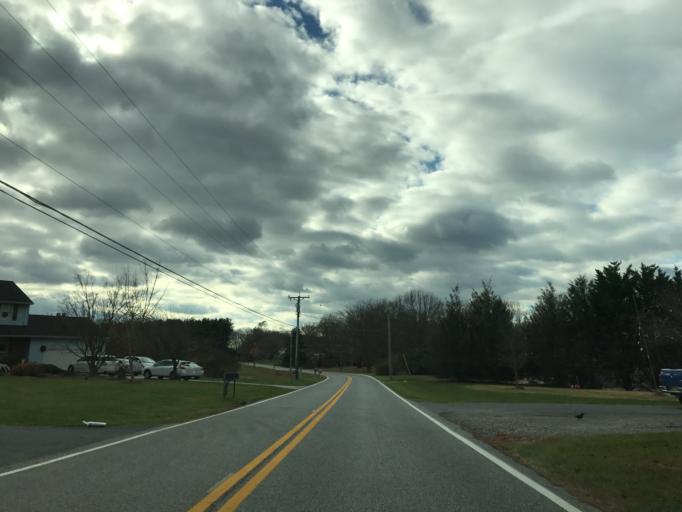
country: US
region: Pennsylvania
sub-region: York County
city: Stewartstown
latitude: 39.6462
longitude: -76.6221
